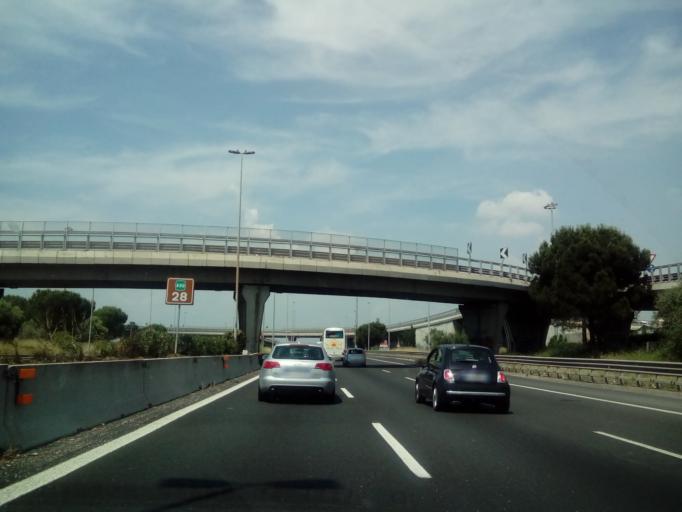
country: IT
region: Latium
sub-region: Citta metropolitana di Roma Capitale
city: Ciampino
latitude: 41.8212
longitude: 12.5797
